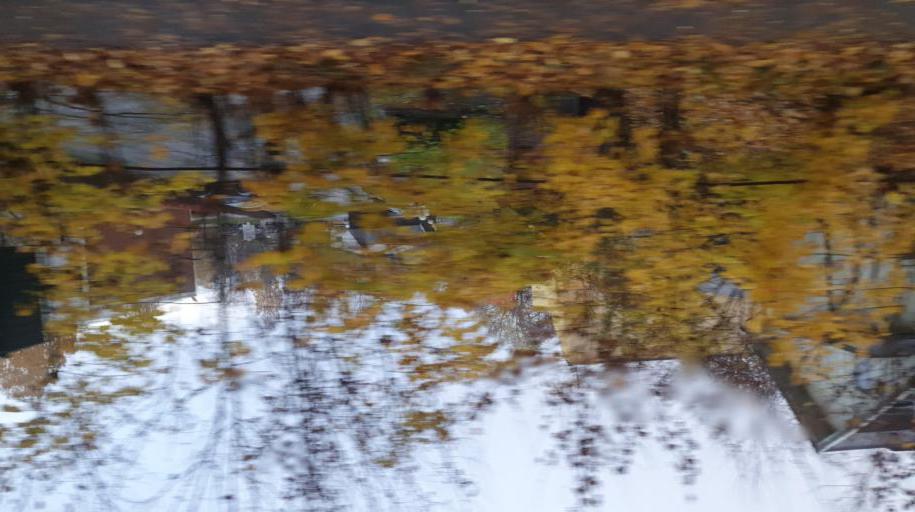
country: NO
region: Buskerud
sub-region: Drammen
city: Drammen
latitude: 59.7467
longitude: 10.1632
